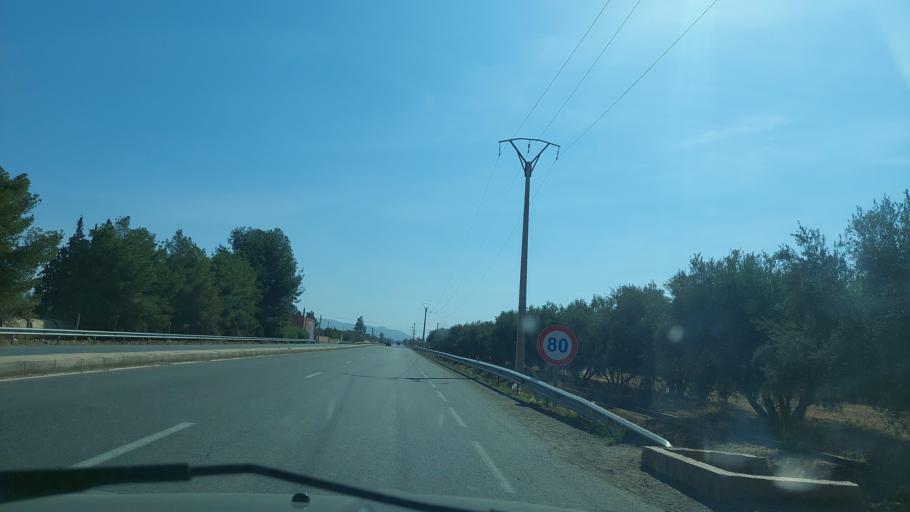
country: MA
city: Sidi Abdallah Ghiat
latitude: 31.5652
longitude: -7.7206
